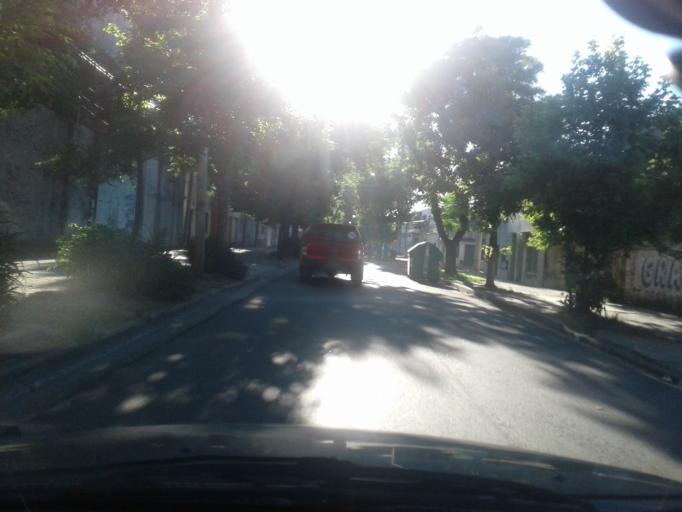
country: AR
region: Santa Fe
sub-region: Departamento de Rosario
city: Rosario
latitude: -32.9481
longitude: -60.6856
